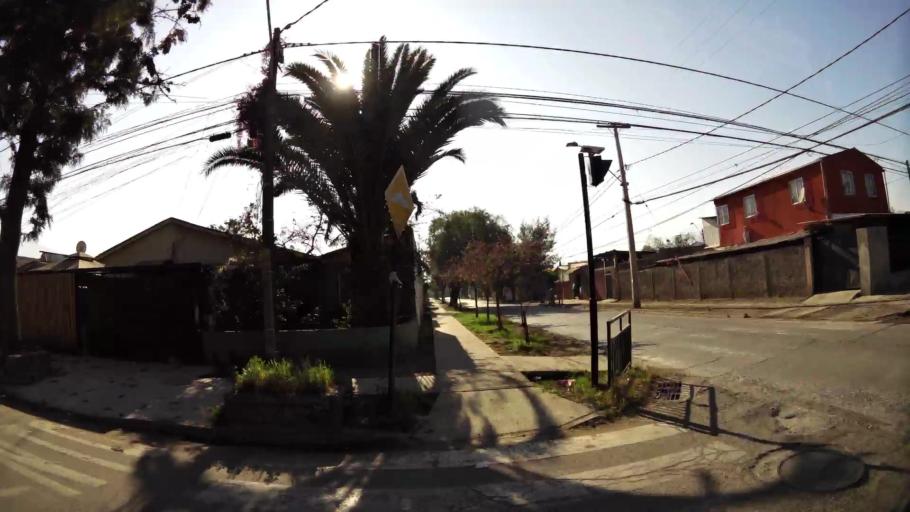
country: CL
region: Santiago Metropolitan
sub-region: Provincia de Santiago
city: Santiago
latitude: -33.3896
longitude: -70.6661
